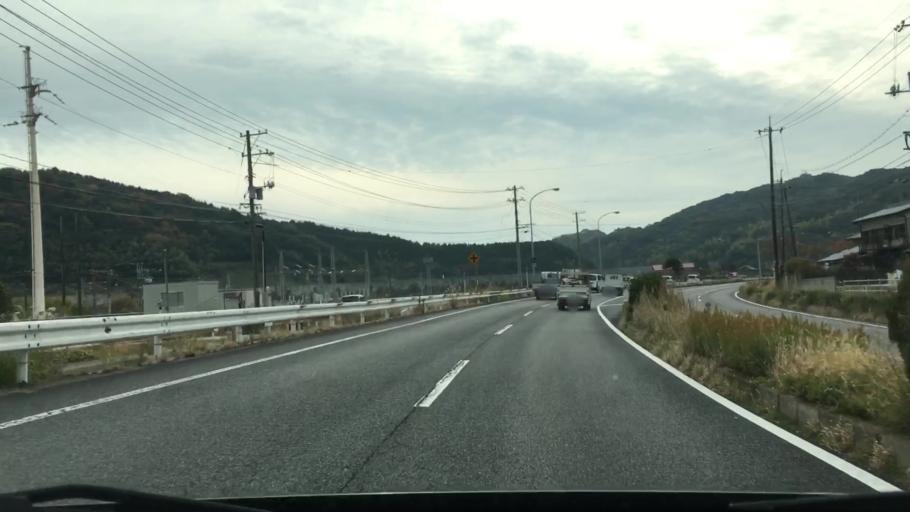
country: JP
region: Yamaguchi
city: Tokuyama
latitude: 34.0702
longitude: 131.7024
